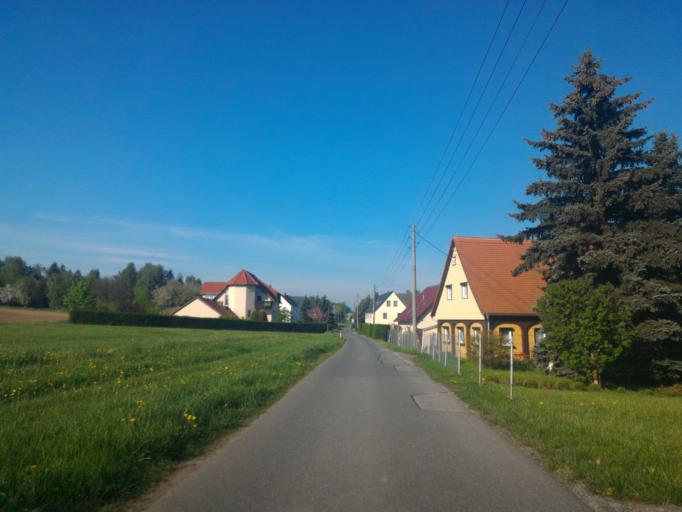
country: DE
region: Saxony
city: Leutersdorf
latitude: 50.9499
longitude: 14.6578
